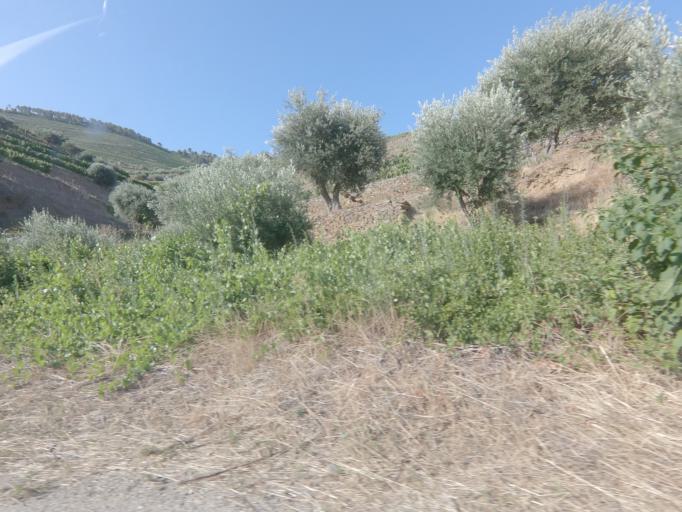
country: PT
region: Viseu
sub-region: Tabuaco
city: Tabuaco
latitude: 41.1758
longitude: -7.5668
